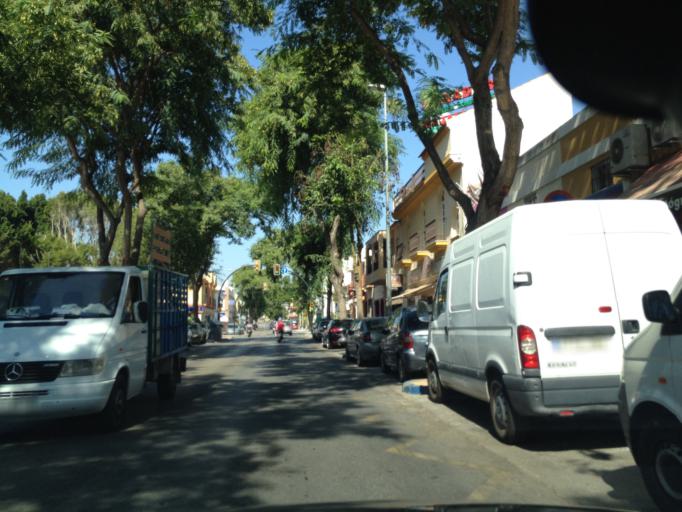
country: ES
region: Andalusia
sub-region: Provincia de Malaga
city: Alhaurin de la Torre
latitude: 36.7235
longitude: -4.5383
